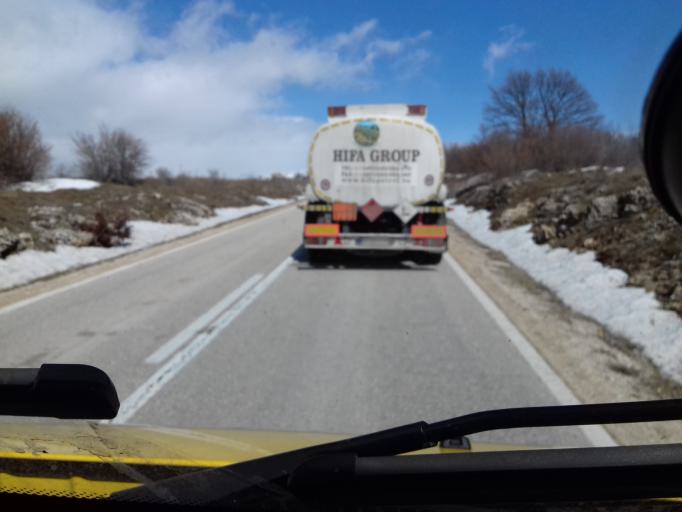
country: BA
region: Federation of Bosnia and Herzegovina
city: Tomislavgrad
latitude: 43.7850
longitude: 17.2226
